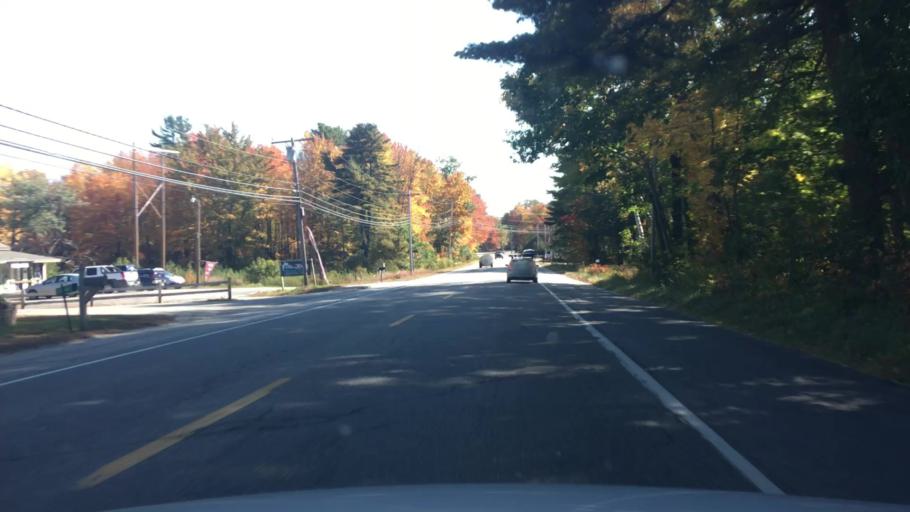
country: US
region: Maine
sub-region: Sagadahoc County
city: Topsham
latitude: 43.9554
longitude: -69.9991
